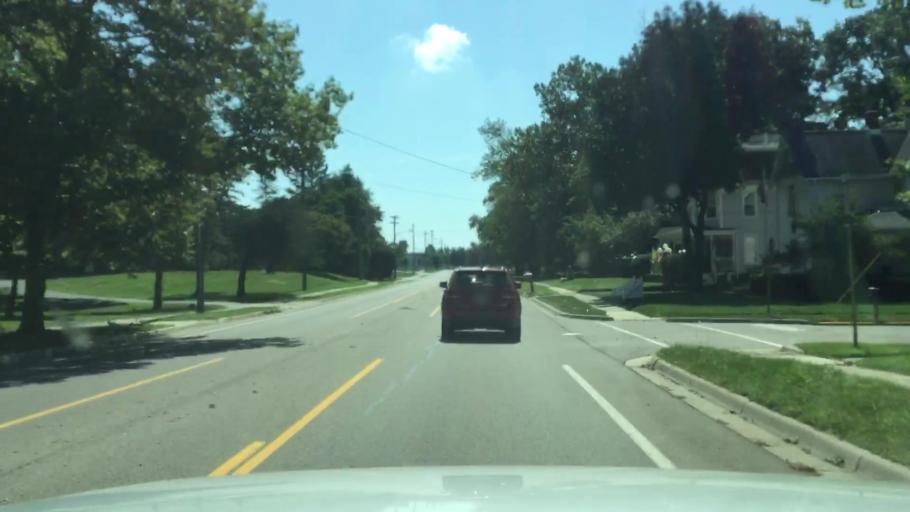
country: US
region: Michigan
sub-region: Lenawee County
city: Clinton
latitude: 42.0684
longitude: -83.9693
